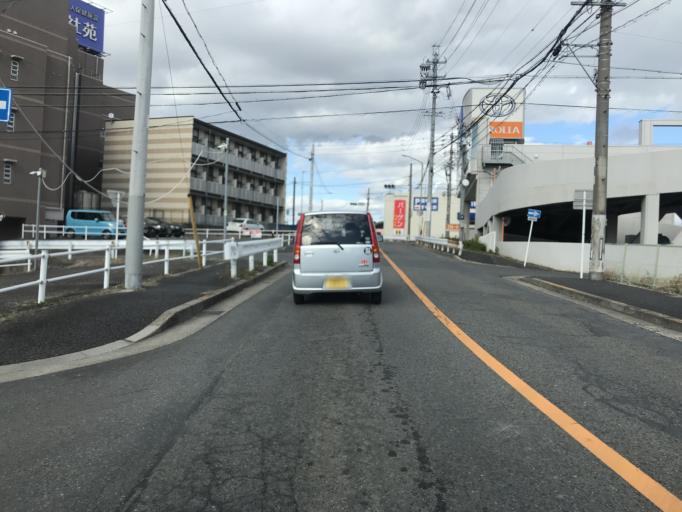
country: JP
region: Aichi
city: Nagoya-shi
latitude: 35.1770
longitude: 136.8492
